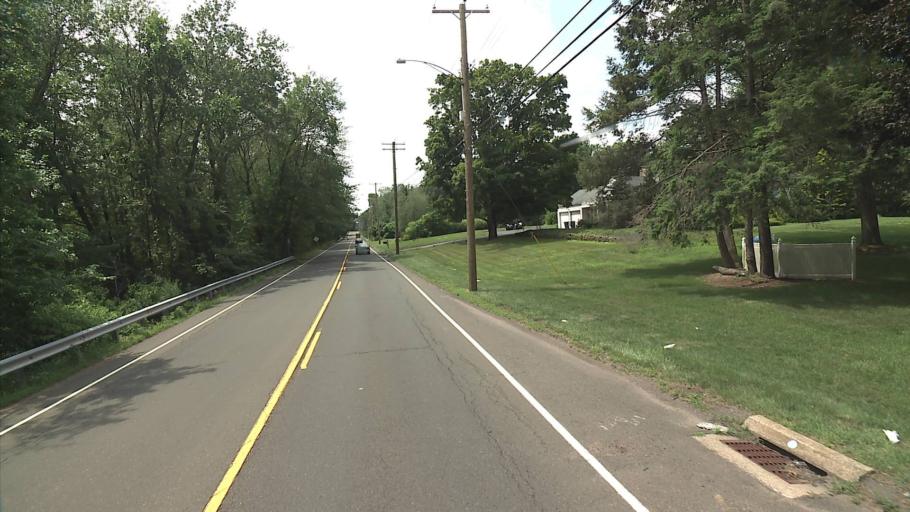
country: US
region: Connecticut
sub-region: New Haven County
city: North Haven
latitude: 41.3665
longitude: -72.8328
